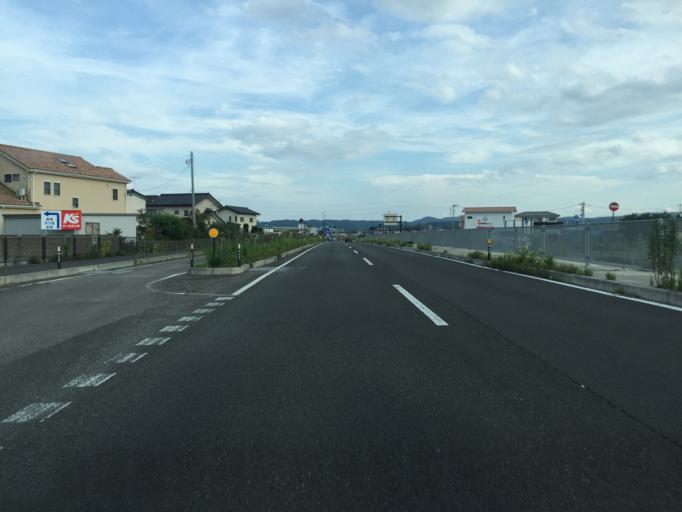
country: JP
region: Fukushima
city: Fukushima-shi
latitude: 37.7360
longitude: 140.4412
